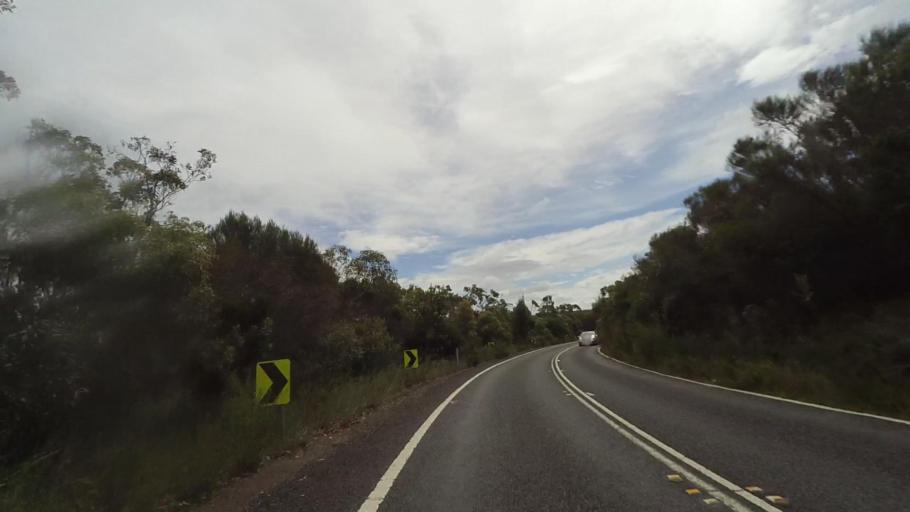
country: AU
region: New South Wales
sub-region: Sutherland Shire
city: Grays Point
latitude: -34.1219
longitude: 151.0770
